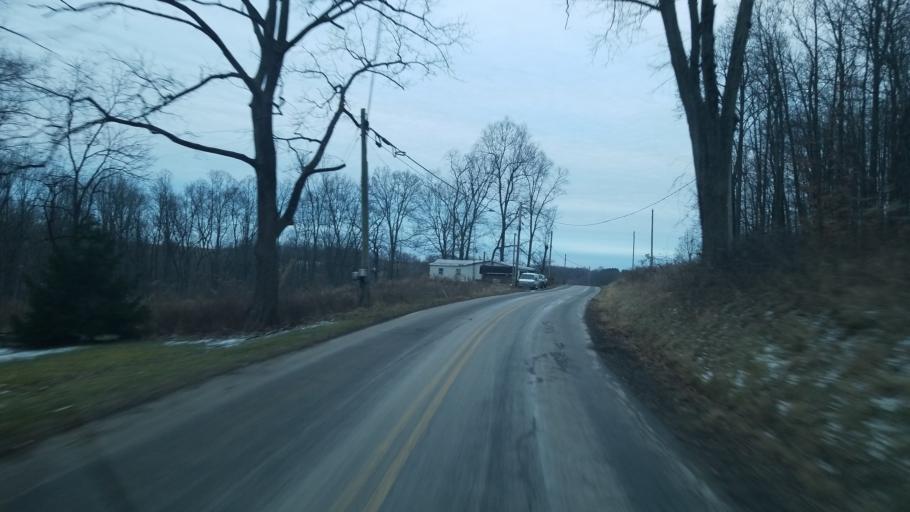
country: US
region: Ohio
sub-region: Holmes County
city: Millersburg
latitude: 40.5047
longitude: -81.8850
